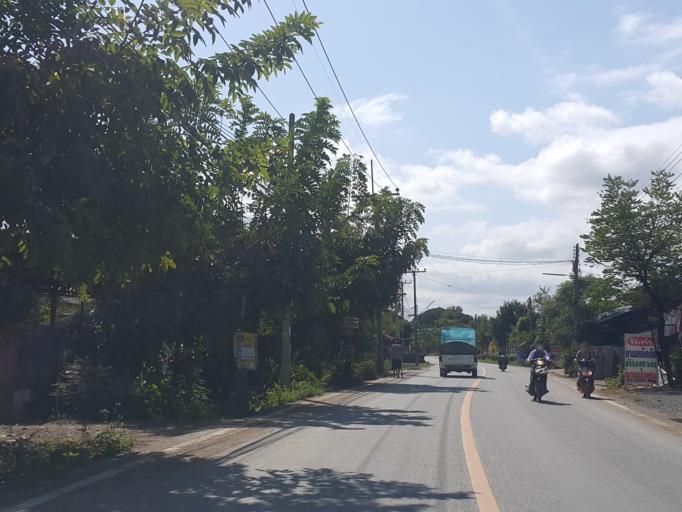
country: TH
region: Chiang Mai
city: San Kamphaeng
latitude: 18.6951
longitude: 99.1596
